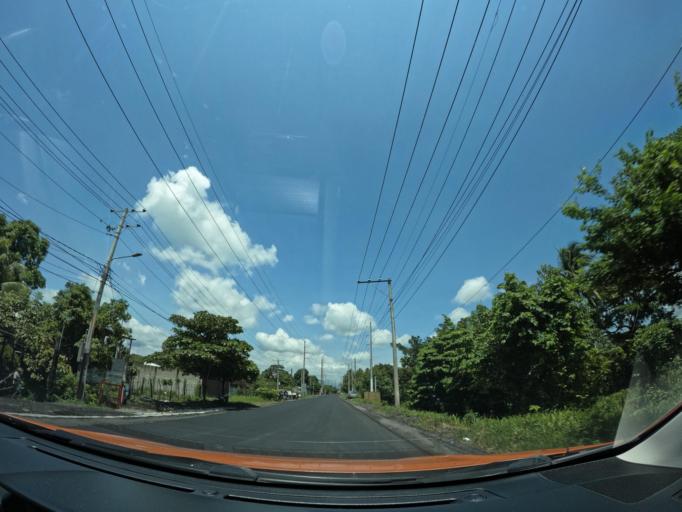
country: GT
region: Escuintla
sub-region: Municipio de Masagua
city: Masagua
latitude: 14.2046
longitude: -90.8427
